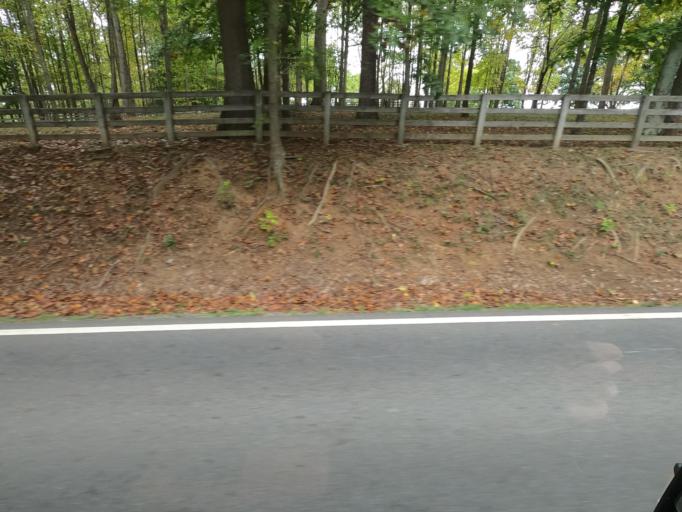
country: US
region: Tennessee
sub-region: Washington County
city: Jonesborough
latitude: 36.2347
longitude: -82.5580
